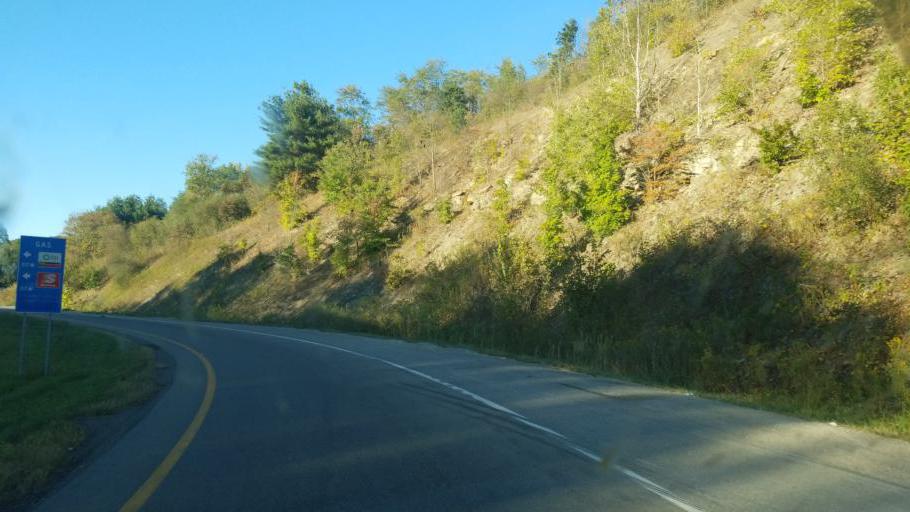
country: US
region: Ohio
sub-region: Tuscarawas County
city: Newcomerstown
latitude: 40.2905
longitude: -81.5548
